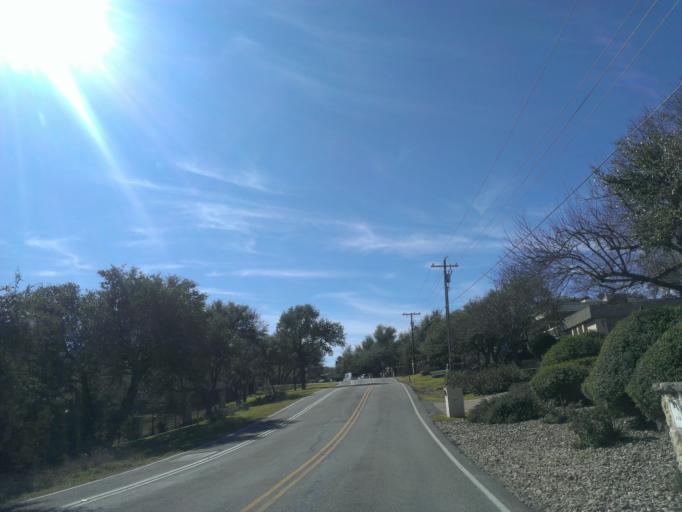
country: US
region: Texas
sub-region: Travis County
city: Lakeway
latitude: 30.3771
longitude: -97.9697
